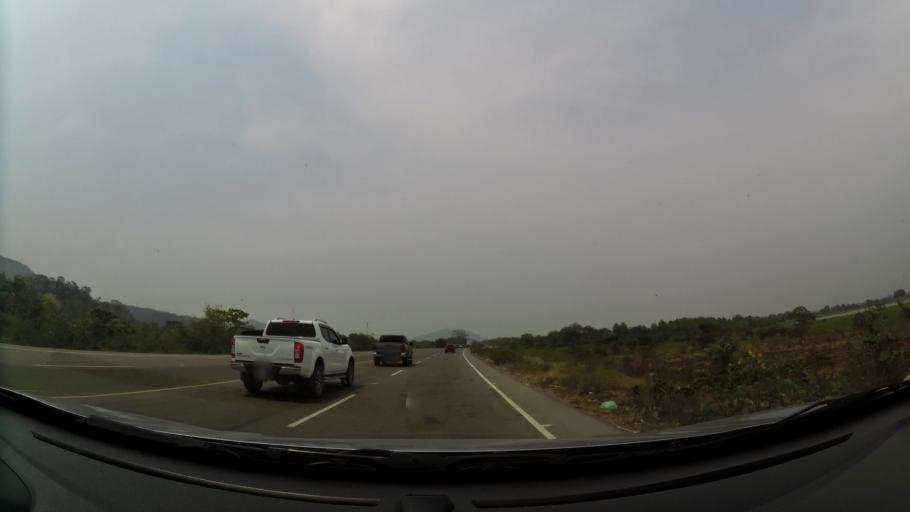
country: HN
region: Cortes
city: Potrerillos
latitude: 15.2207
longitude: -87.9622
